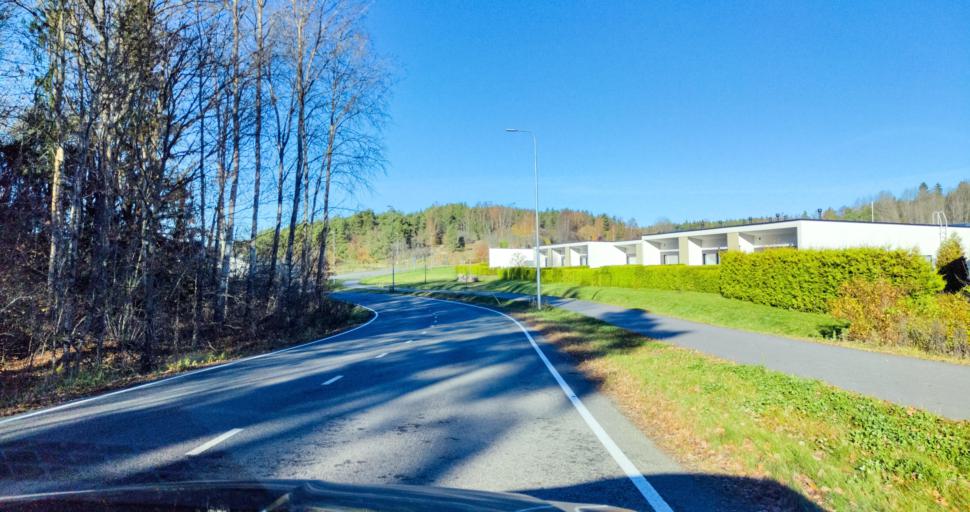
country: FI
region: Varsinais-Suomi
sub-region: Turku
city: Turku
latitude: 60.4096
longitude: 22.2095
